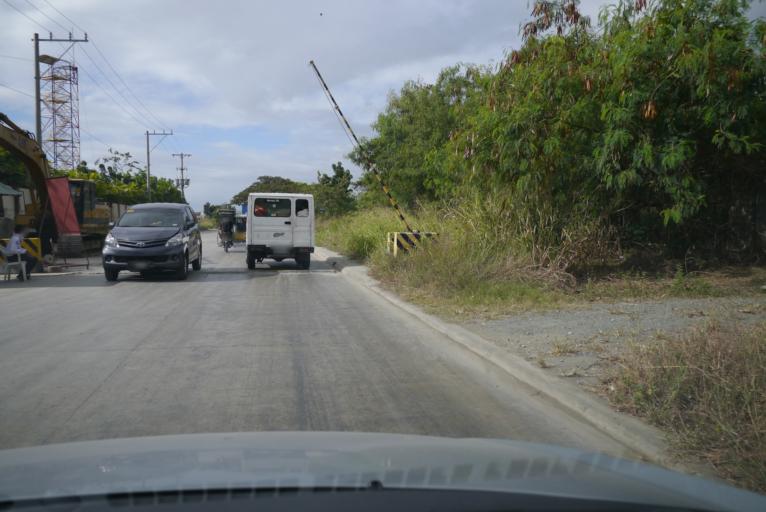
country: PH
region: Calabarzon
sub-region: Province of Rizal
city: Taytay
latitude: 14.5490
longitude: 121.1297
